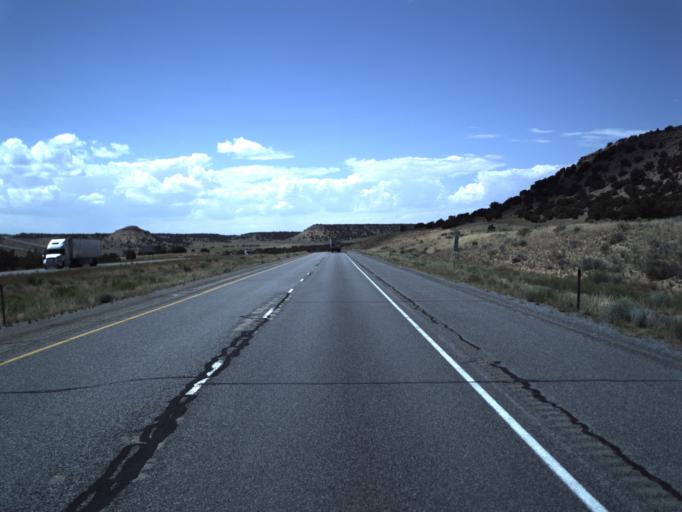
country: US
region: Utah
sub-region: Emery County
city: Castle Dale
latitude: 38.9052
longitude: -110.5441
